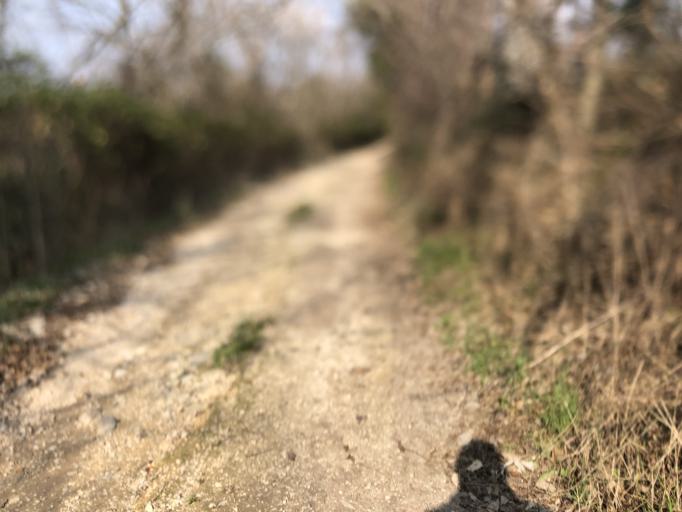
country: IT
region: Veneto
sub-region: Provincia di Verona
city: Sona
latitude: 45.4294
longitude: 10.8364
